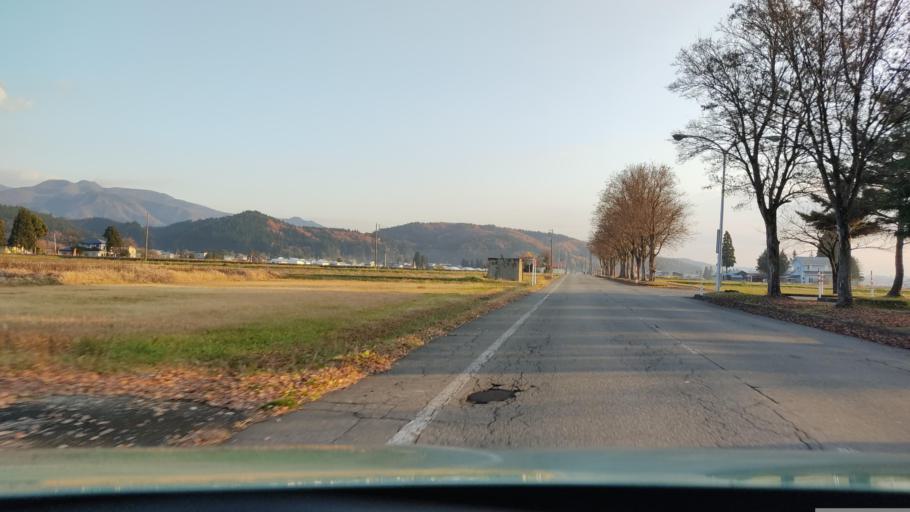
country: JP
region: Akita
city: Omagari
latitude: 39.4617
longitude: 140.5837
